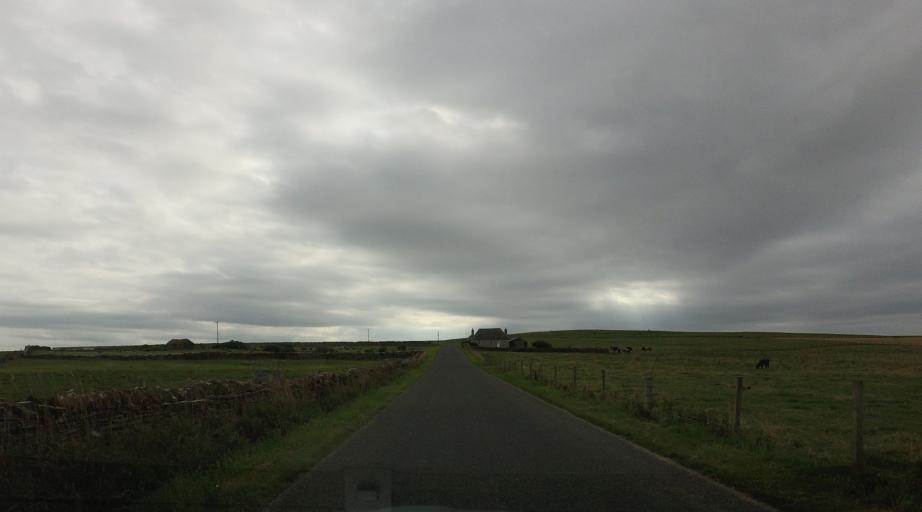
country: GB
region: Scotland
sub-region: Orkney Islands
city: Stromness
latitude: 59.0316
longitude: -3.3141
